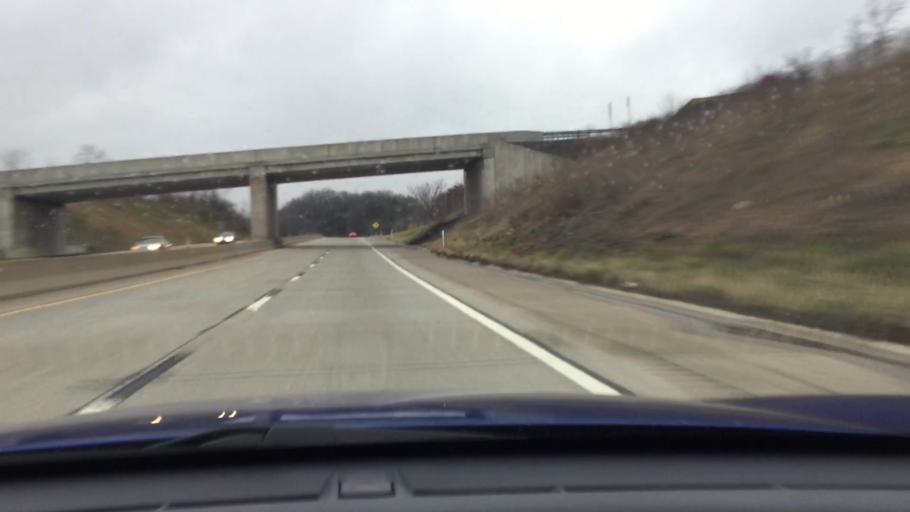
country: US
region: Pennsylvania
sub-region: Allegheny County
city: Imperial
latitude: 40.4307
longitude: -80.2632
